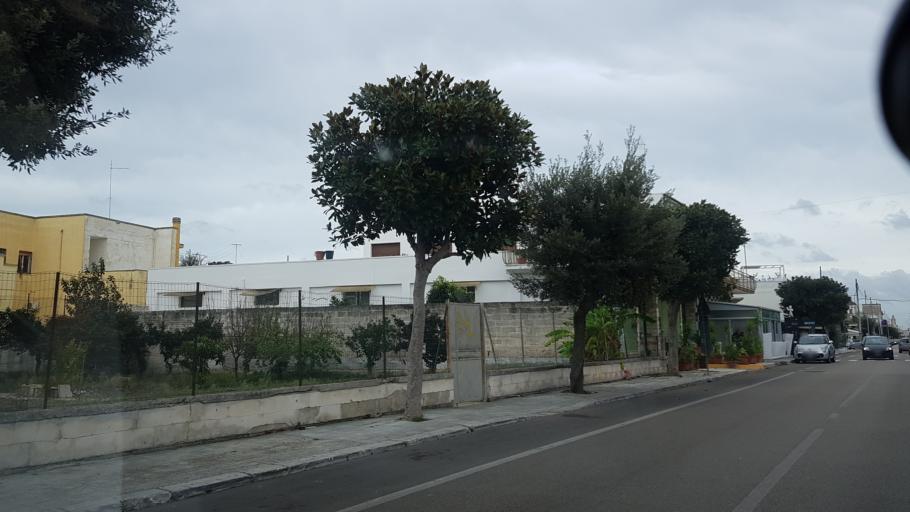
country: IT
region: Apulia
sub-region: Provincia di Lecce
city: Guagnano
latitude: 40.4005
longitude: 17.9441
